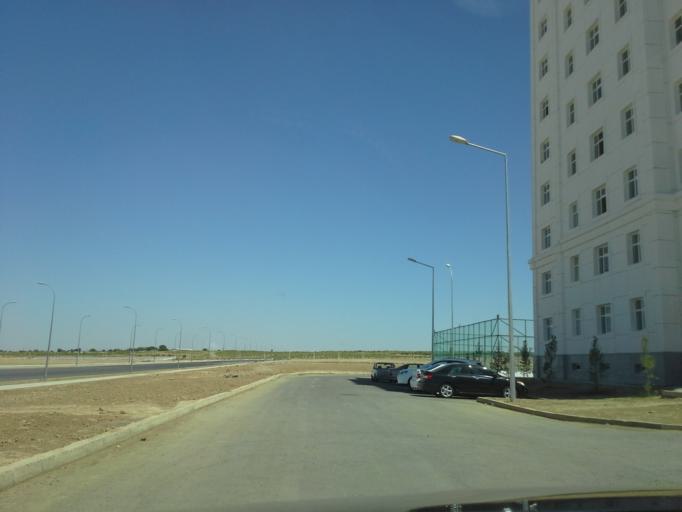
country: TM
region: Ahal
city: Ashgabat
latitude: 37.8898
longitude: 58.4116
